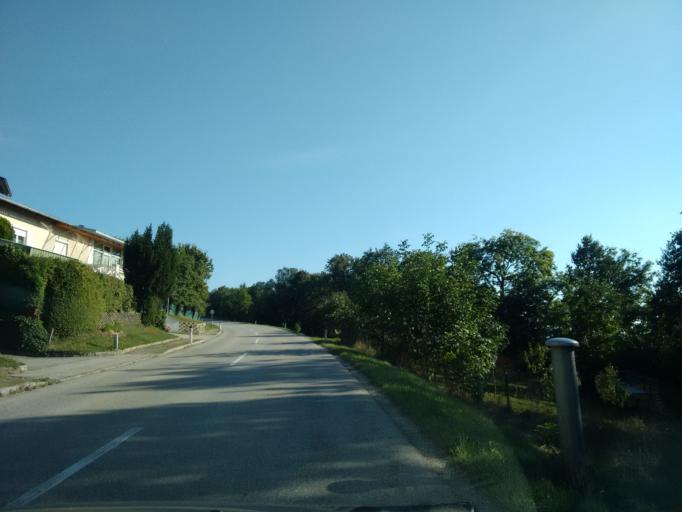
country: AT
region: Upper Austria
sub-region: Wels-Land
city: Marchtrenk
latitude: 48.1584
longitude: 14.1246
